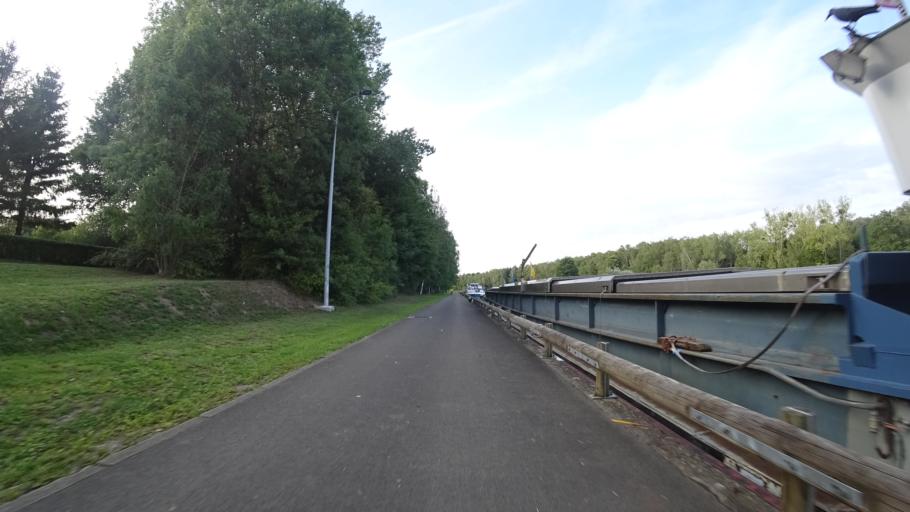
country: BE
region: Wallonia
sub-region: Province de Namur
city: Fosses-la-Ville
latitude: 50.4453
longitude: 4.7068
